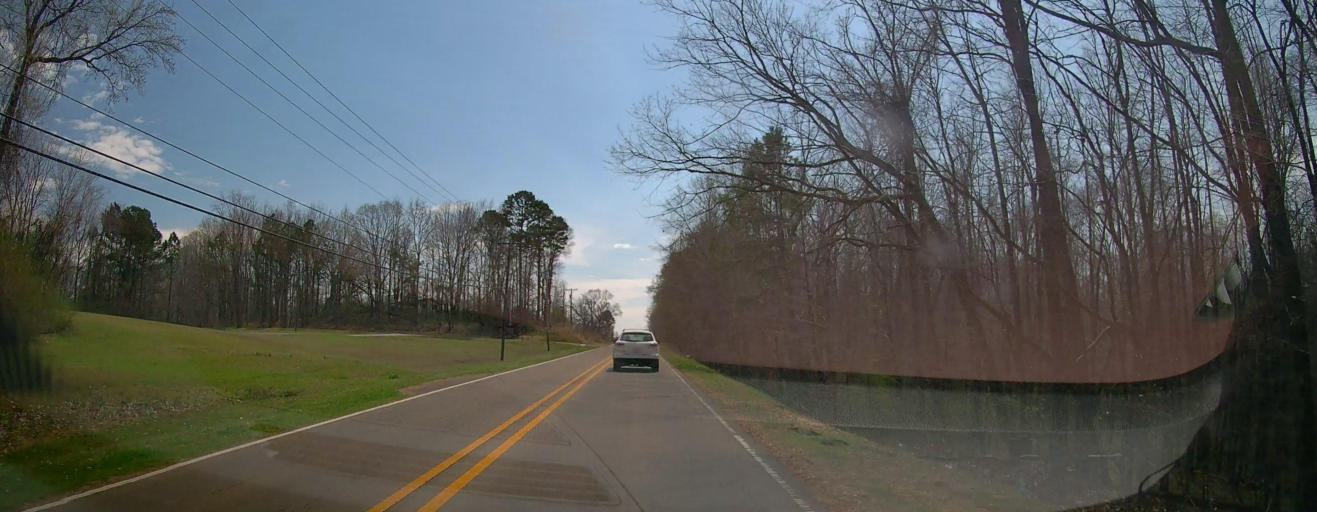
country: US
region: Mississippi
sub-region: Union County
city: New Albany
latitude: 34.4631
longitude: -88.9808
